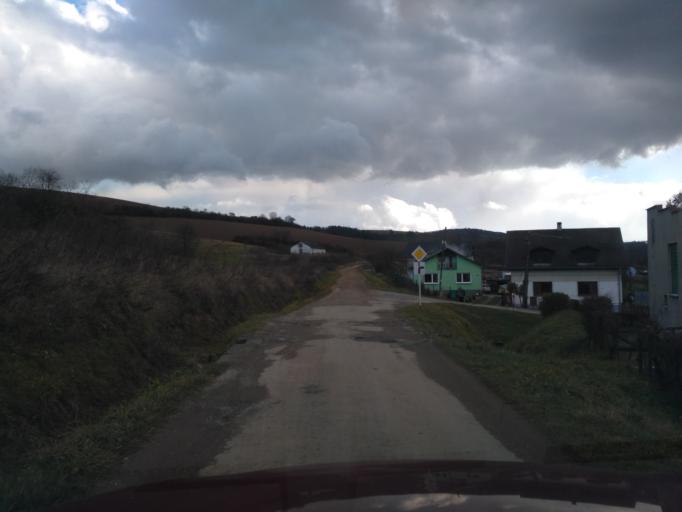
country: SK
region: Presovsky
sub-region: Okres Presov
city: Presov
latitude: 48.9314
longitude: 21.1920
